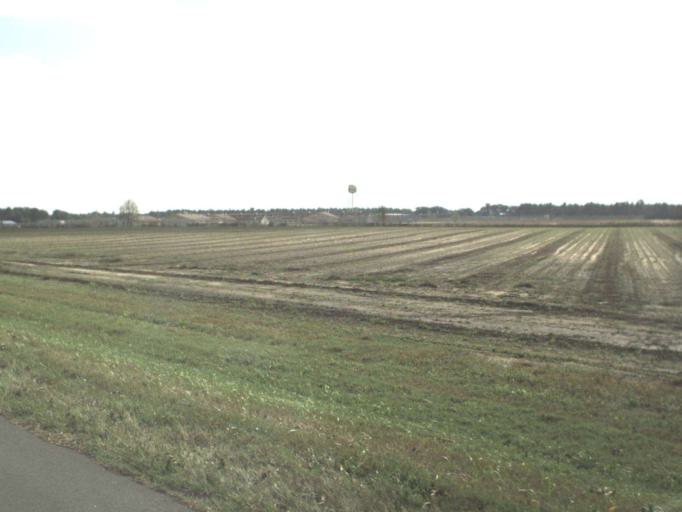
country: US
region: Florida
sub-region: Jackson County
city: Malone
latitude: 30.9765
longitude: -85.1713
